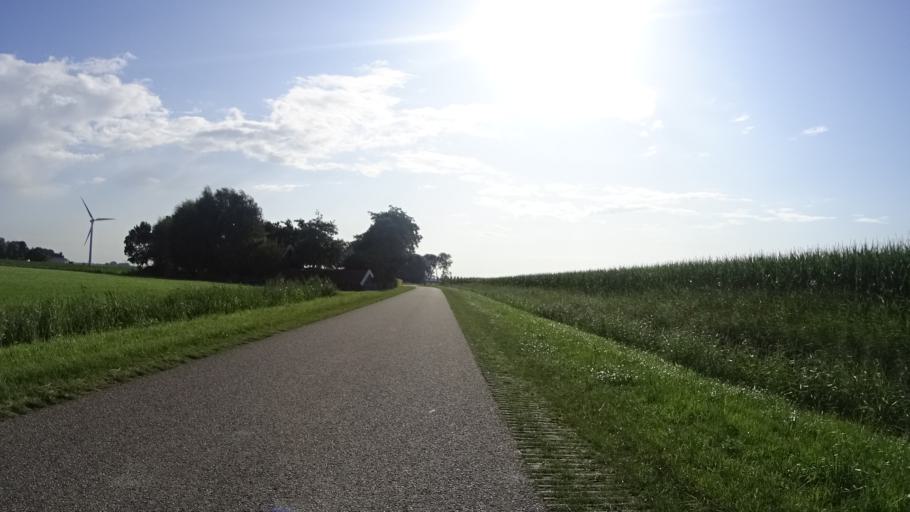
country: NL
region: Friesland
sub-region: Gemeente Harlingen
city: Harlingen
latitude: 53.1197
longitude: 5.4275
